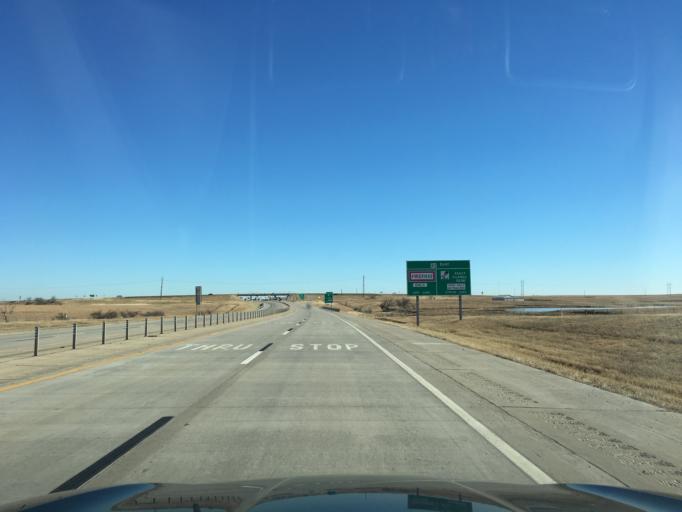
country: US
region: Oklahoma
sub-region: Noble County
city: Perry
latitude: 36.3840
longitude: -97.0763
